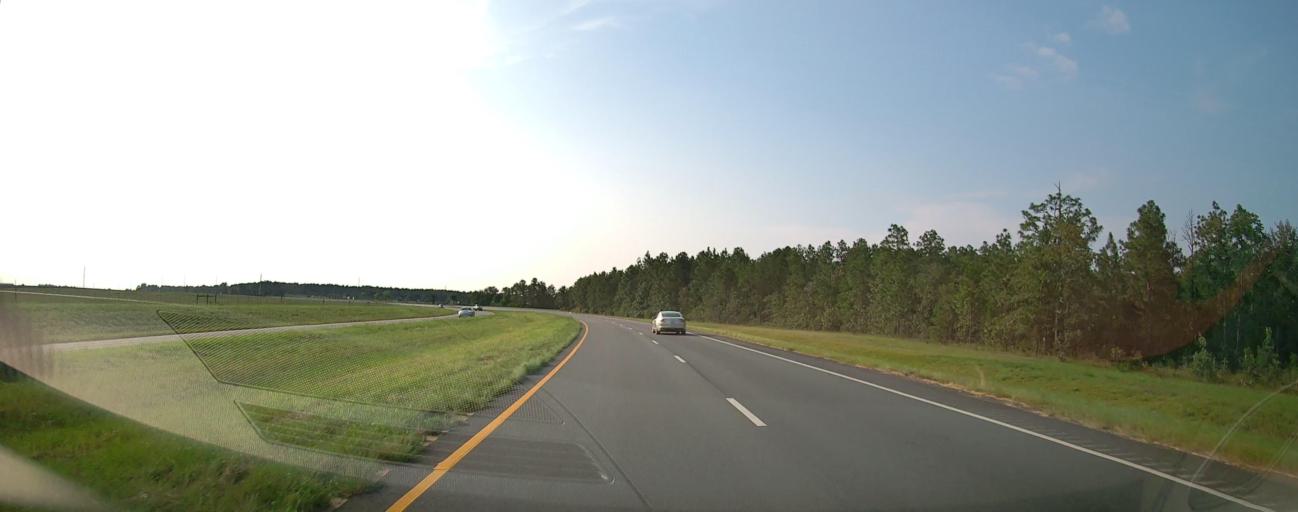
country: US
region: Georgia
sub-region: Taylor County
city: Butler
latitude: 32.5635
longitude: -84.2684
